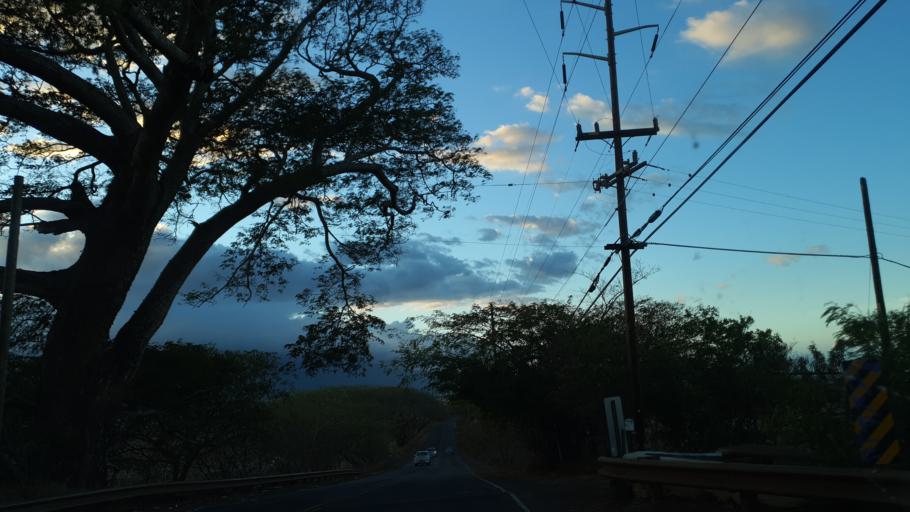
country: US
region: Hawaii
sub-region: Maui County
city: Kahului
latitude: 20.8651
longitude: -156.4316
